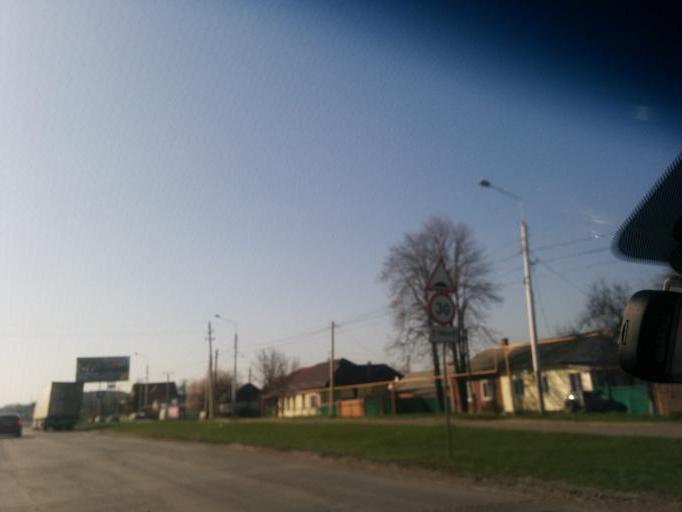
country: RU
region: Rostov
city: Shakhty
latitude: 47.7103
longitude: 40.1726
